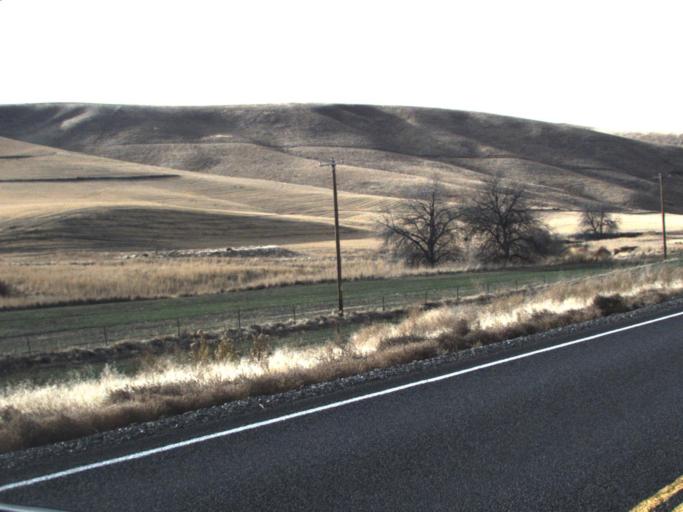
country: US
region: Washington
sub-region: Garfield County
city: Pomeroy
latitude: 46.4739
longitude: -117.7251
